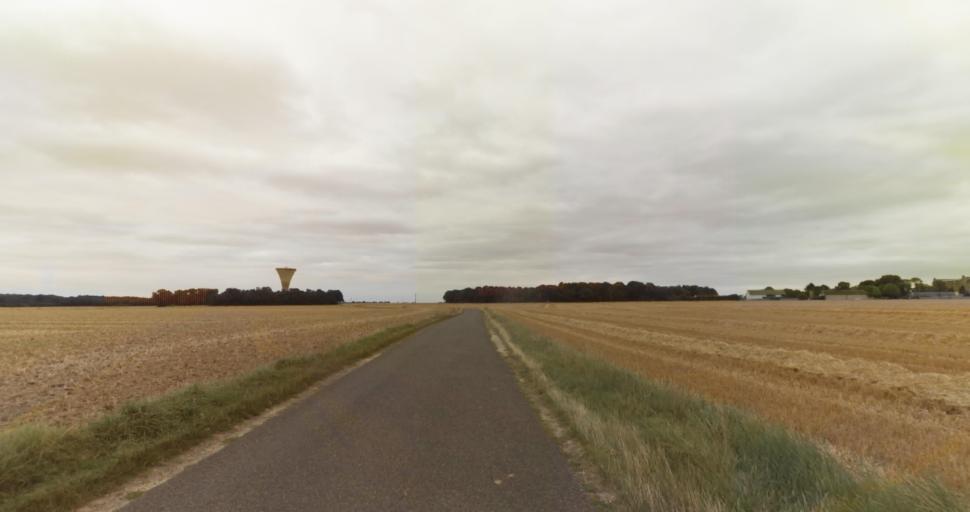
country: FR
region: Haute-Normandie
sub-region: Departement de l'Eure
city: Marcilly-sur-Eure
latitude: 48.9322
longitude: 1.2873
